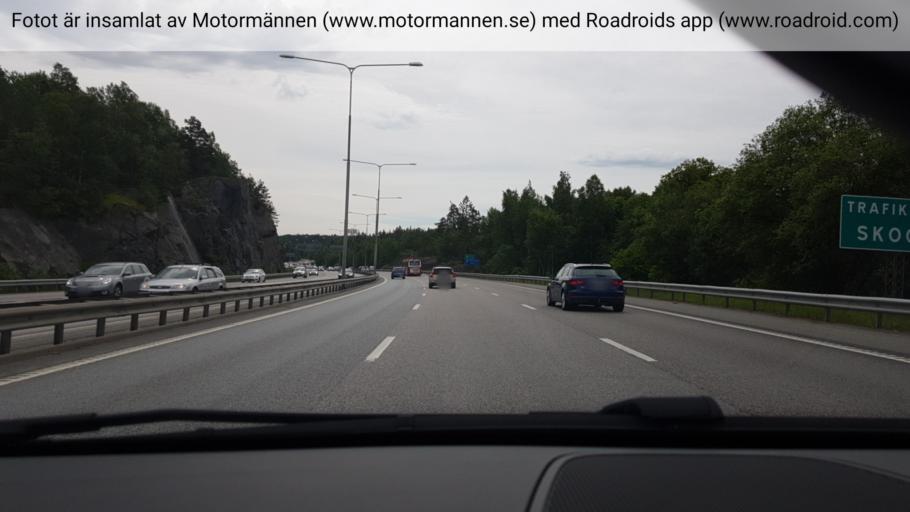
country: SE
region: Stockholm
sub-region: Haninge Kommun
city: Handen
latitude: 59.2270
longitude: 18.1261
